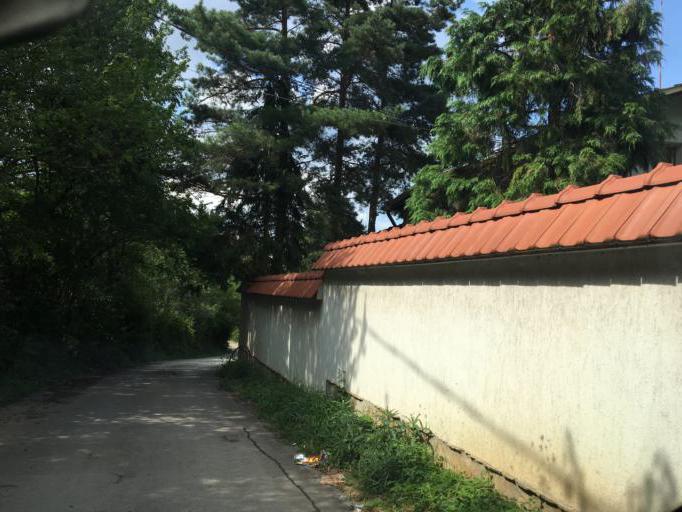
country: BG
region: Sofia-Capital
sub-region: Stolichna Obshtina
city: Sofia
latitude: 42.6061
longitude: 23.3661
